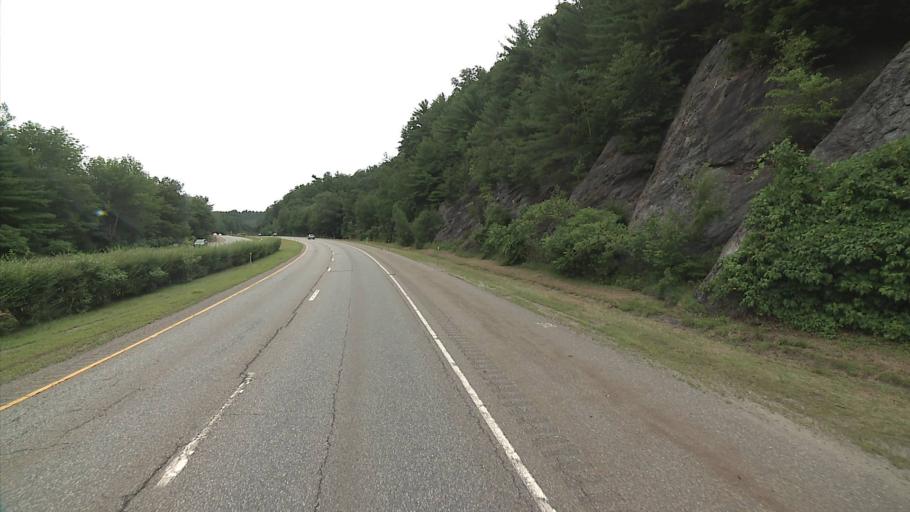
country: US
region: Connecticut
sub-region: Litchfield County
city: Northwest Harwinton
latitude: 41.7521
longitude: -73.1117
